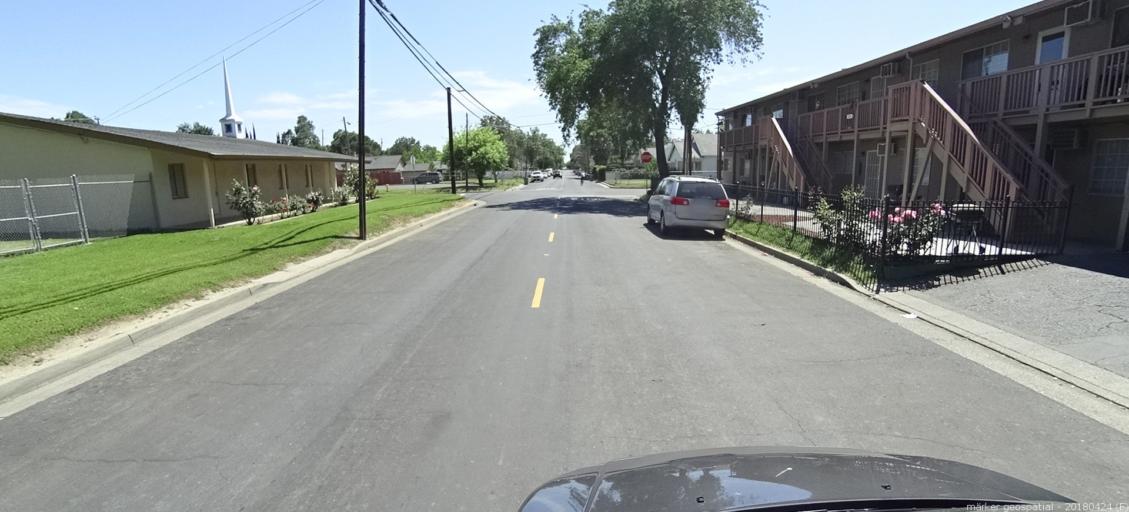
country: US
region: California
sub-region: Yolo County
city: West Sacramento
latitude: 38.5839
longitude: -121.5382
